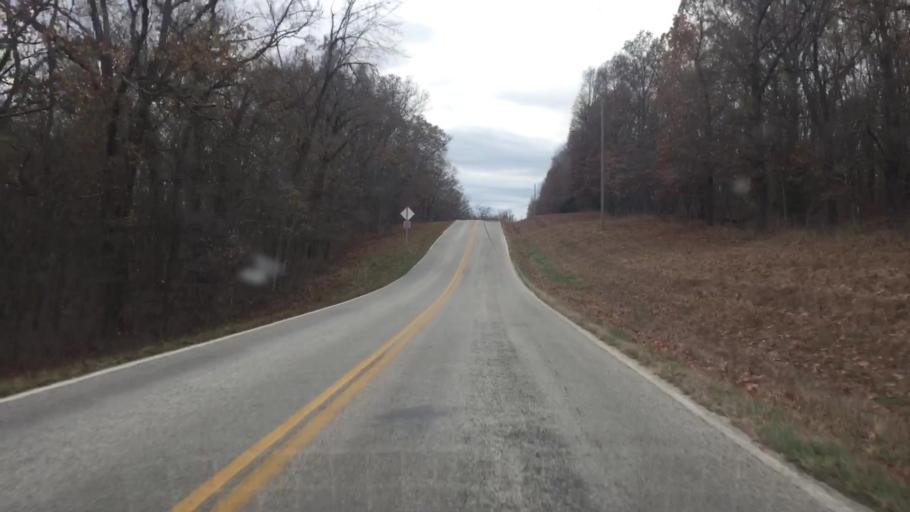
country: US
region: Missouri
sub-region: Saint Clair County
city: Osceola
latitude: 37.9887
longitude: -93.6328
